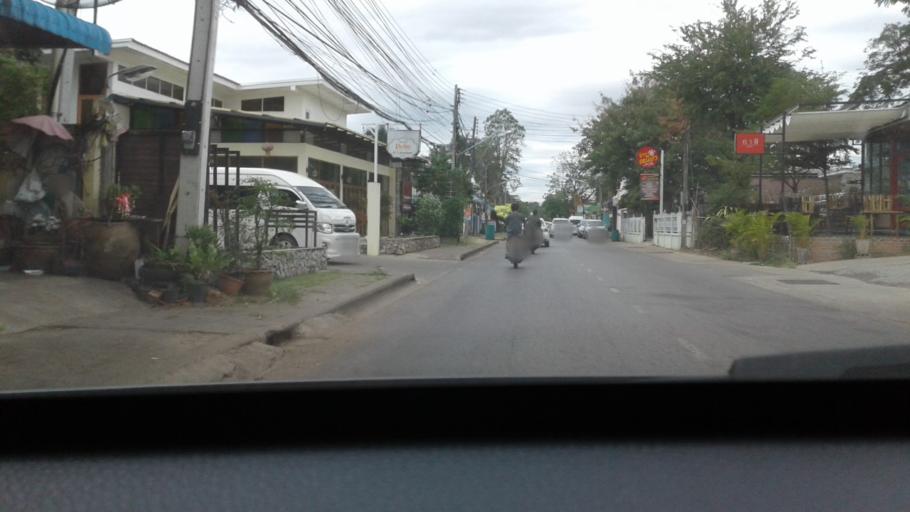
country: TH
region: Changwat Udon Thani
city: Udon Thani
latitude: 17.3974
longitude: 102.7870
